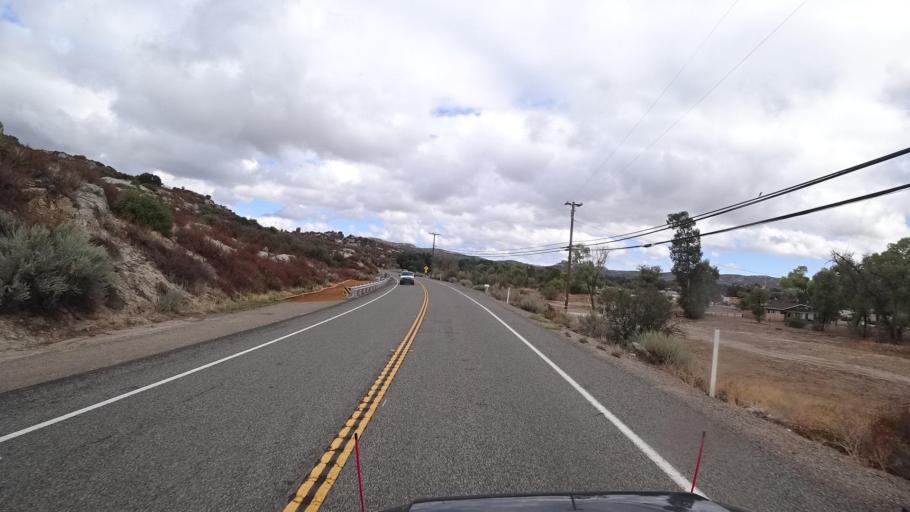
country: US
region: California
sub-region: San Diego County
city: Campo
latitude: 32.6353
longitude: -116.4324
